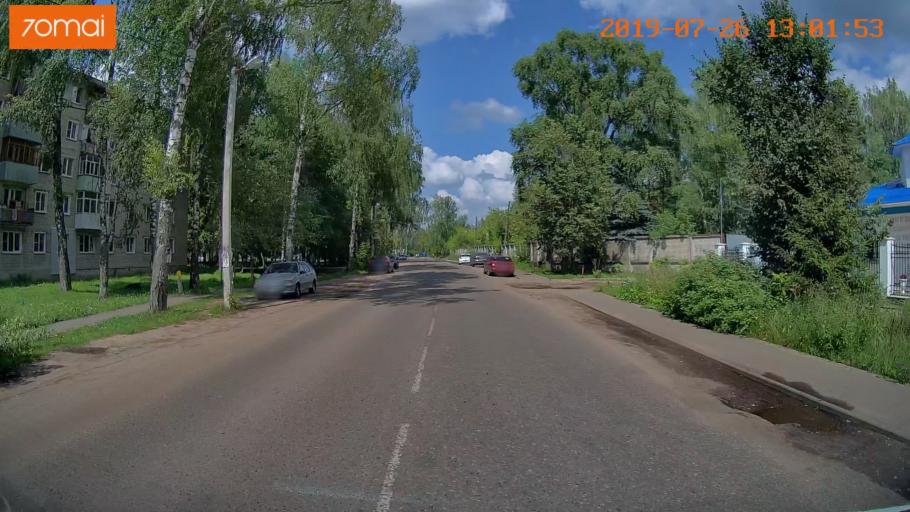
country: RU
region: Ivanovo
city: Bogorodskoye
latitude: 57.0411
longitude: 41.0122
